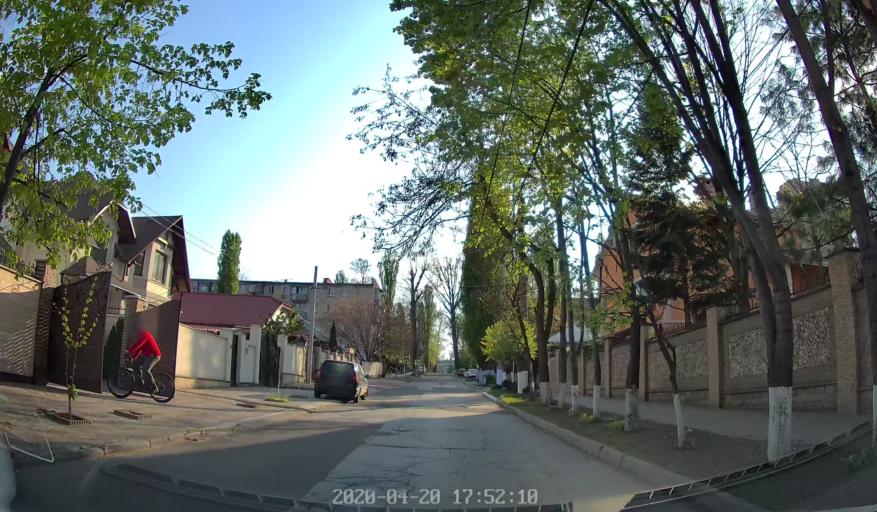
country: MD
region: Chisinau
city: Chisinau
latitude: 46.9990
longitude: 28.8639
